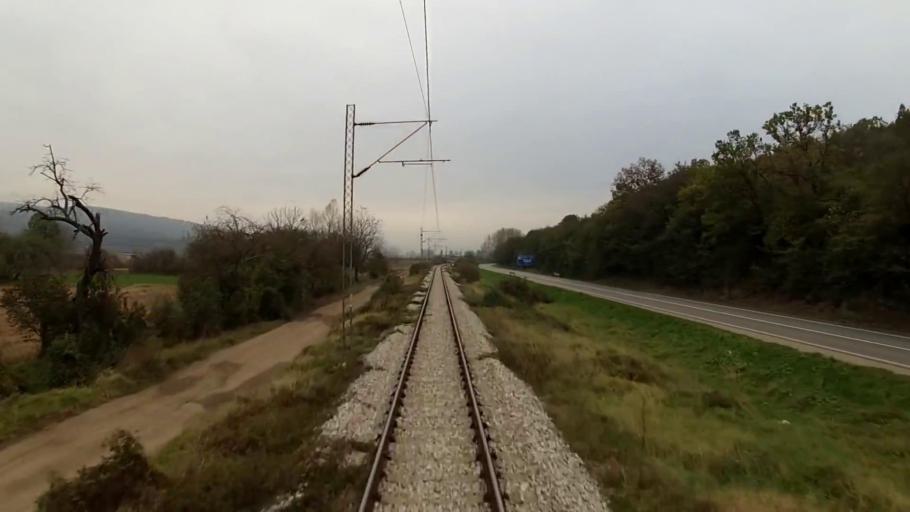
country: RS
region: Central Serbia
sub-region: Pirotski Okrug
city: Dimitrovgrad
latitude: 43.0117
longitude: 22.7989
